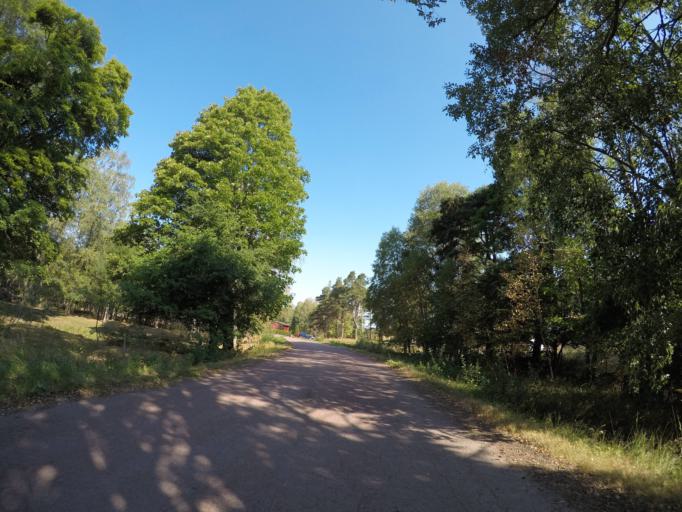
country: AX
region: Alands landsbygd
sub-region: Finstroem
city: Finstroem
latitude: 60.2719
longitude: 19.9399
